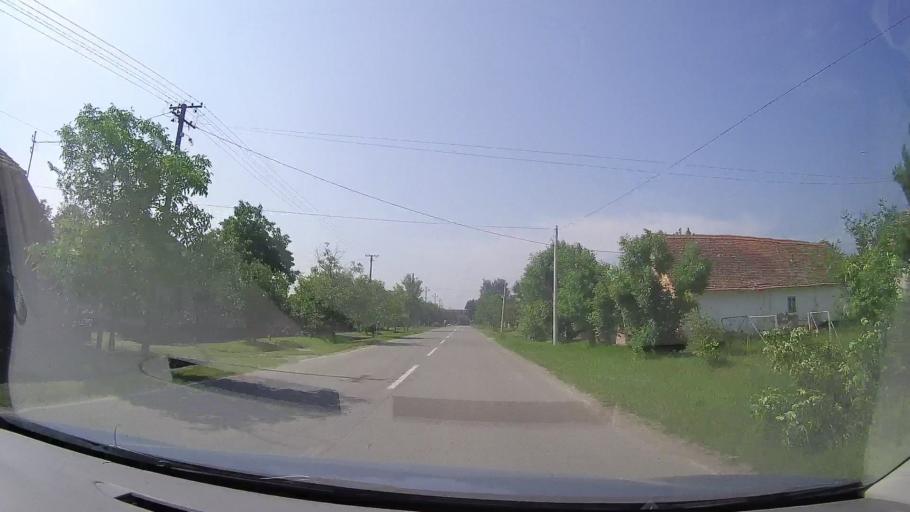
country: RS
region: Autonomna Pokrajina Vojvodina
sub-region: Srednjebanatski Okrug
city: Secanj
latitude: 45.3702
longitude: 20.7773
